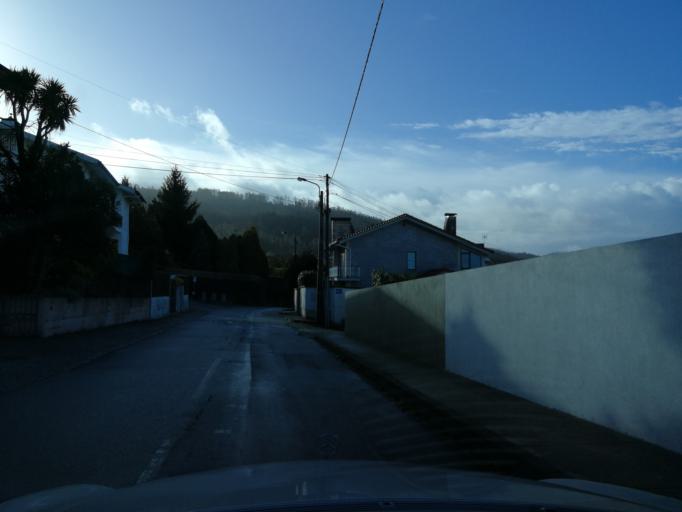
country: PT
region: Braga
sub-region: Braga
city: Braga
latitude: 41.5476
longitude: -8.3897
